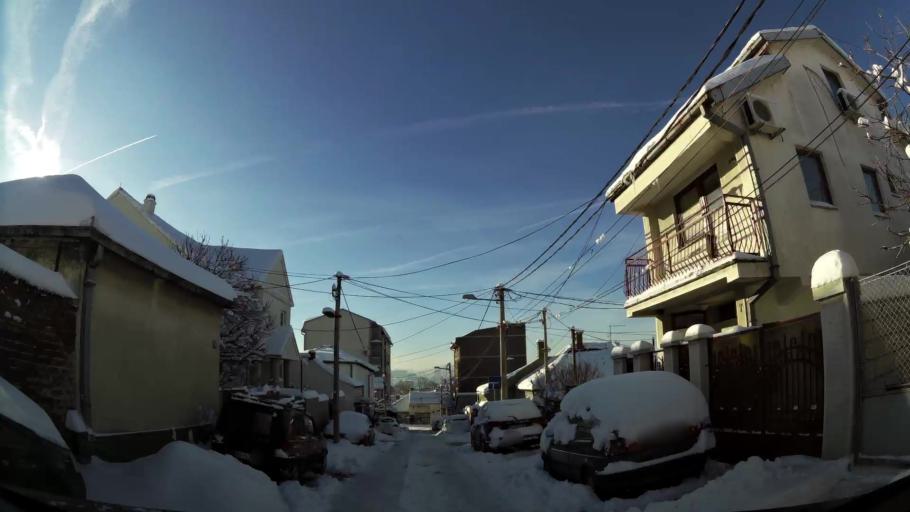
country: RS
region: Central Serbia
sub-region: Belgrade
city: Vracar
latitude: 44.7884
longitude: 20.4939
